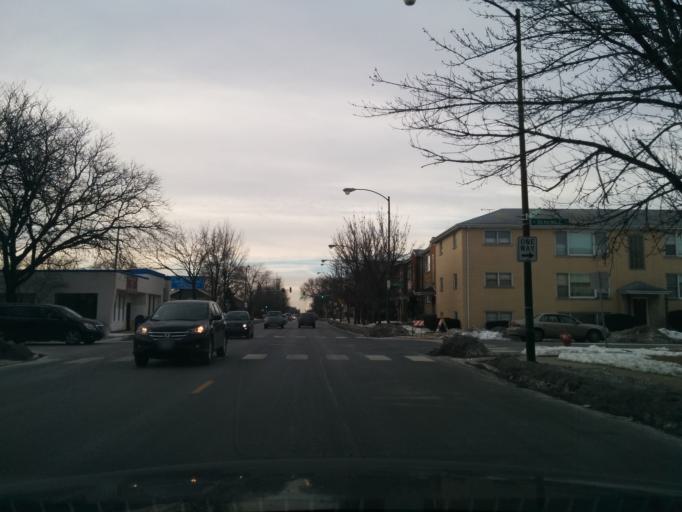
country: US
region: Illinois
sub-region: Cook County
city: Harwood Heights
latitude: 41.9507
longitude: -87.7670
